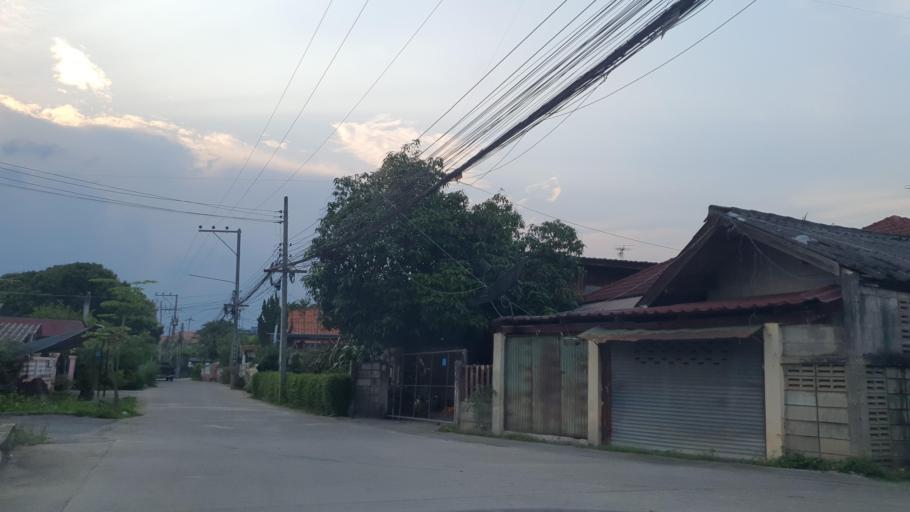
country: TH
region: Chiang Mai
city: Hang Dong
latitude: 18.6658
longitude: 98.9300
